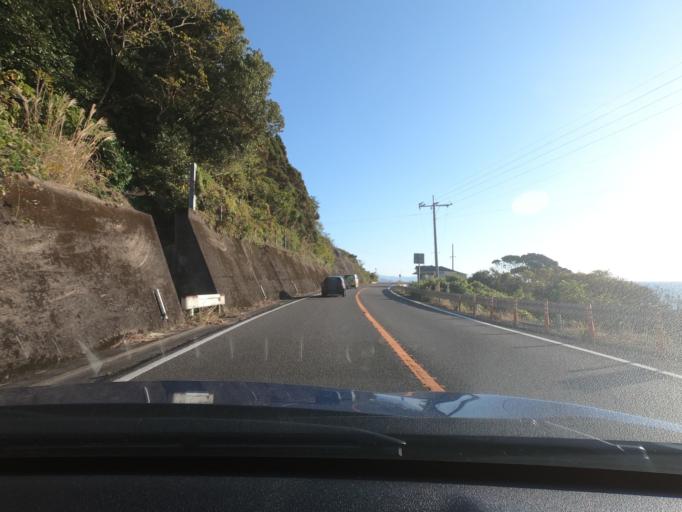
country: JP
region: Kagoshima
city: Akune
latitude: 31.9593
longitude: 130.2143
